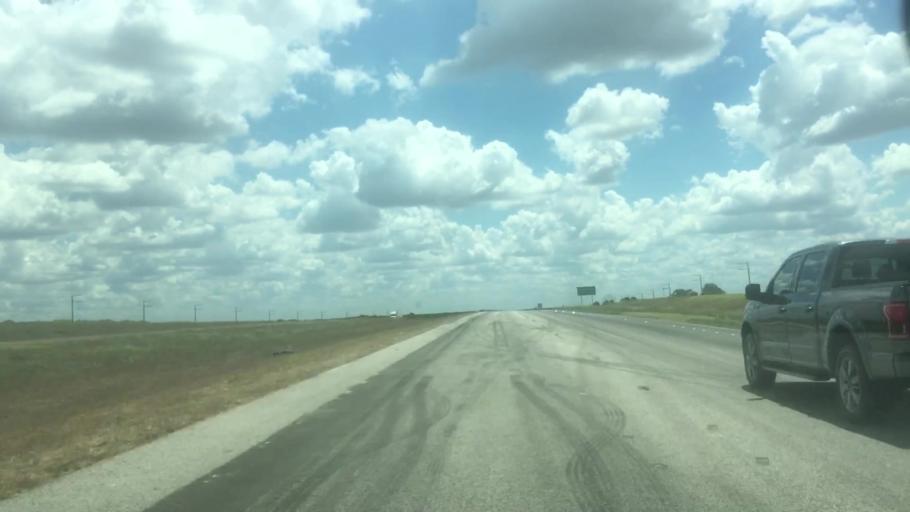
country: US
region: Texas
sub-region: Caldwell County
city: Lockhart
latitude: 29.9824
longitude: -97.6817
